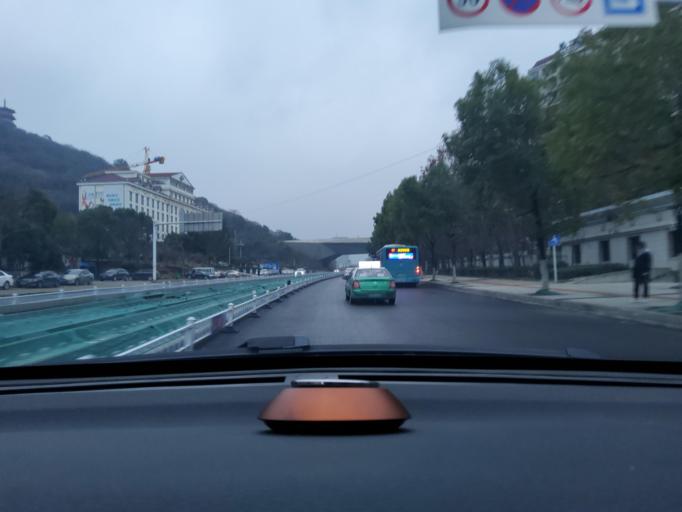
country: CN
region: Hubei
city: Tuanchengshan
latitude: 30.1950
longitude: 115.0204
